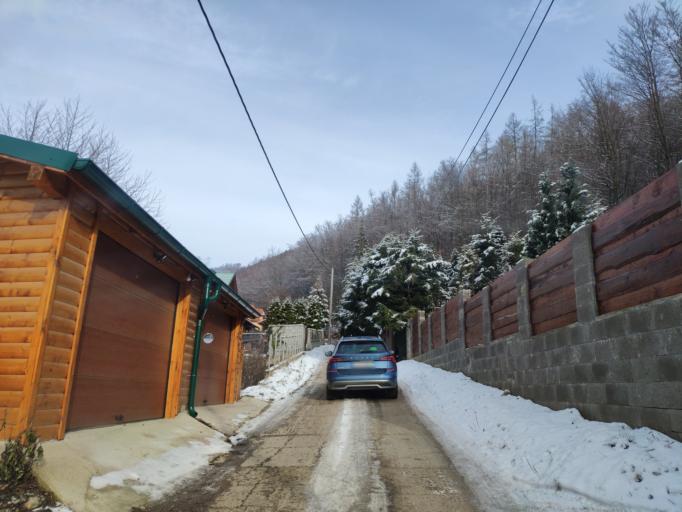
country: SK
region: Kosicky
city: Gelnica
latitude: 48.7584
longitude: 20.9890
